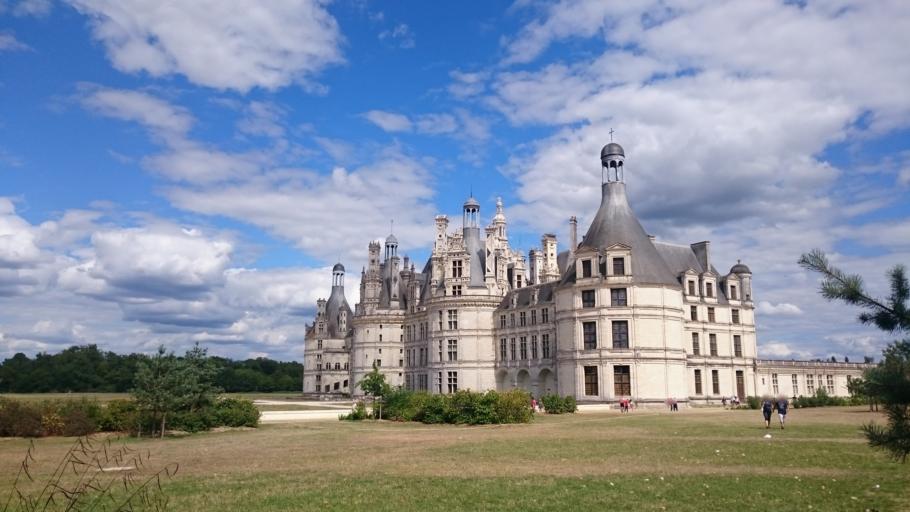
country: FR
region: Centre
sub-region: Departement du Loir-et-Cher
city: Saint-Dye-sur-Loire
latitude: 47.6160
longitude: 1.5146
